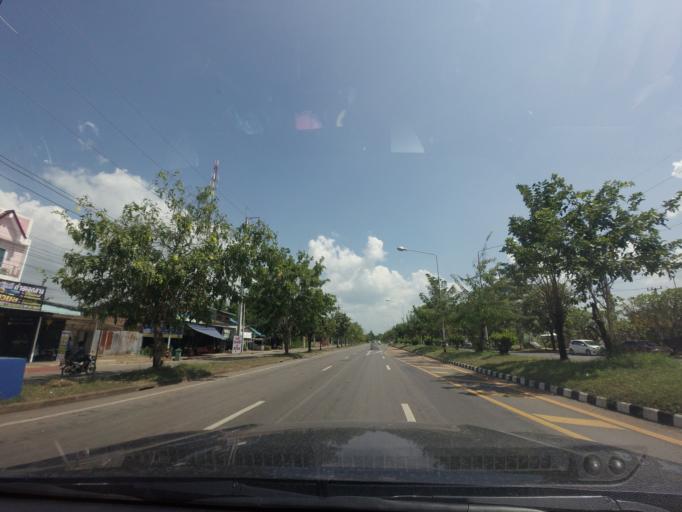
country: TH
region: Phetchabun
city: Nong Phai
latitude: 16.0792
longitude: 101.0608
